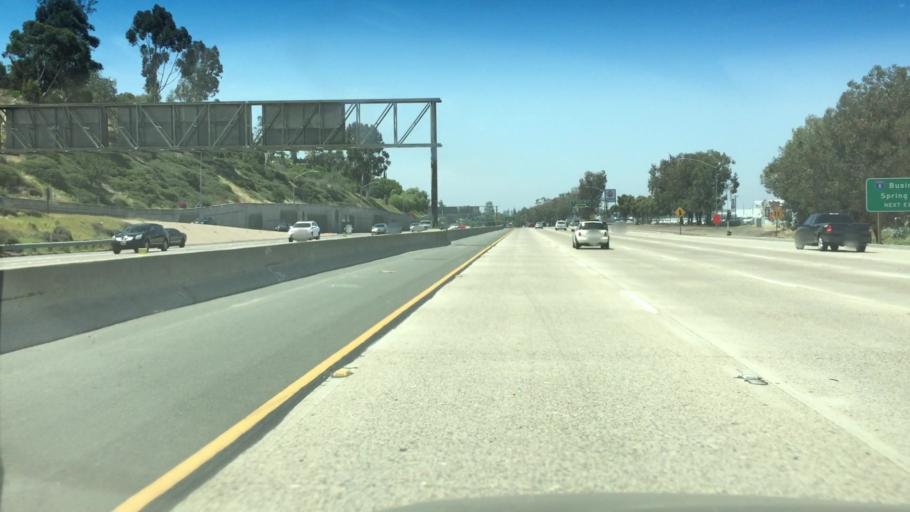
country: US
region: California
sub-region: San Diego County
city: La Mesa
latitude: 32.7745
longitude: -117.0124
